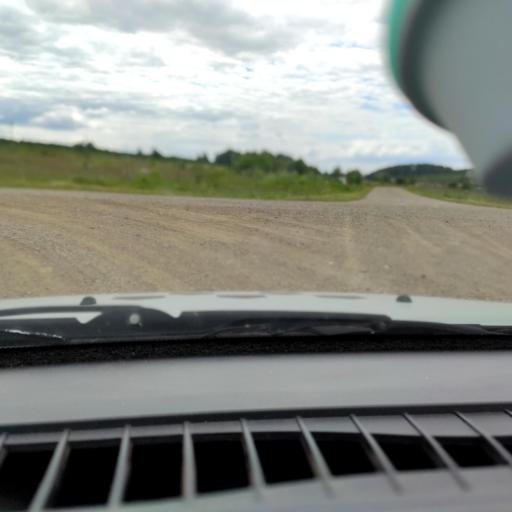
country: RU
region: Perm
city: Suksun
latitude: 57.1905
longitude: 57.5528
